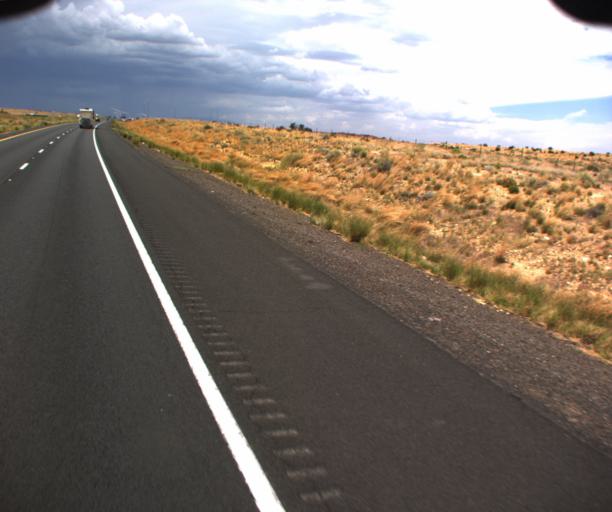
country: US
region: Arizona
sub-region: Coconino County
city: LeChee
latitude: 35.1009
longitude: -110.9823
